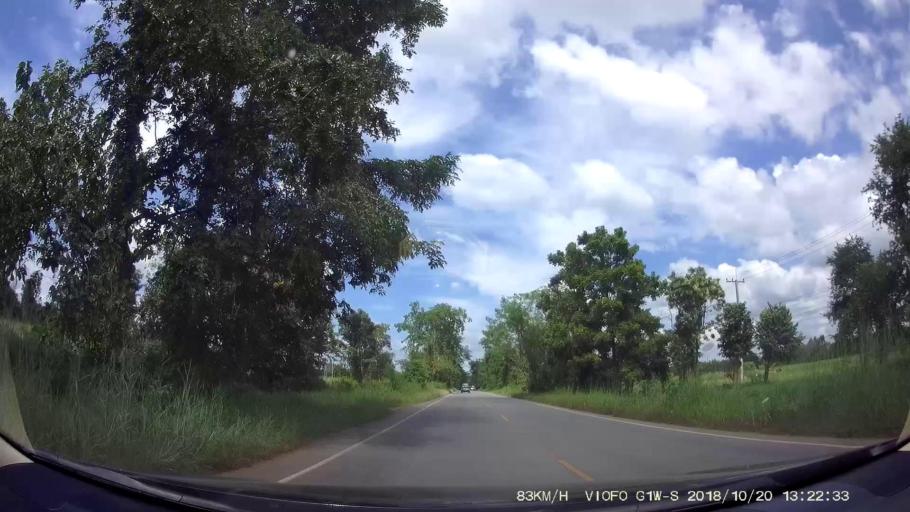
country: TH
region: Chaiyaphum
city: Khon San
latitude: 16.5731
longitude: 101.9164
